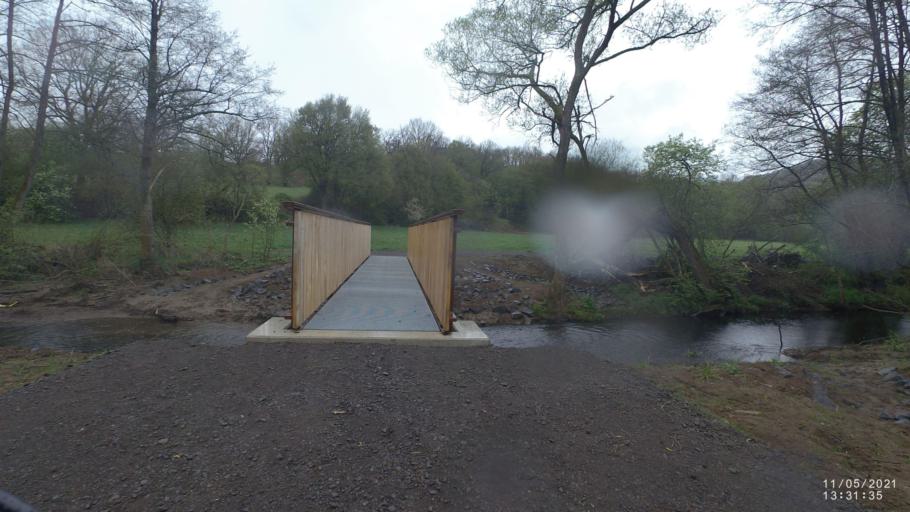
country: DE
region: Rheinland-Pfalz
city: Reudelsterz
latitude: 50.2974
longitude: 7.1419
